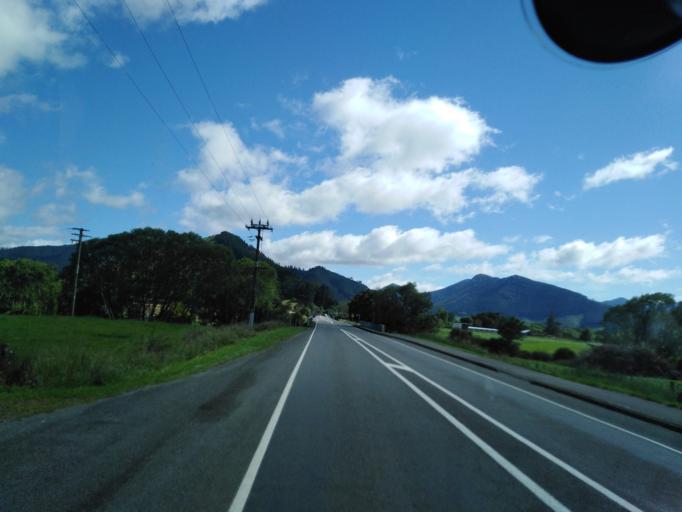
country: NZ
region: Nelson
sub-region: Nelson City
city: Nelson
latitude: -41.2333
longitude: 173.5813
